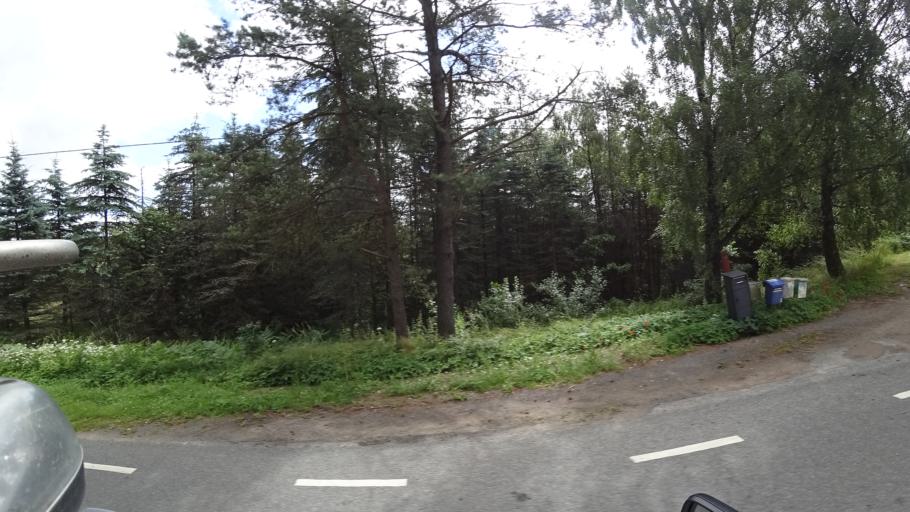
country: SE
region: Skane
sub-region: Kristianstads Kommun
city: Degeberga
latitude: 55.7270
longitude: 13.9999
